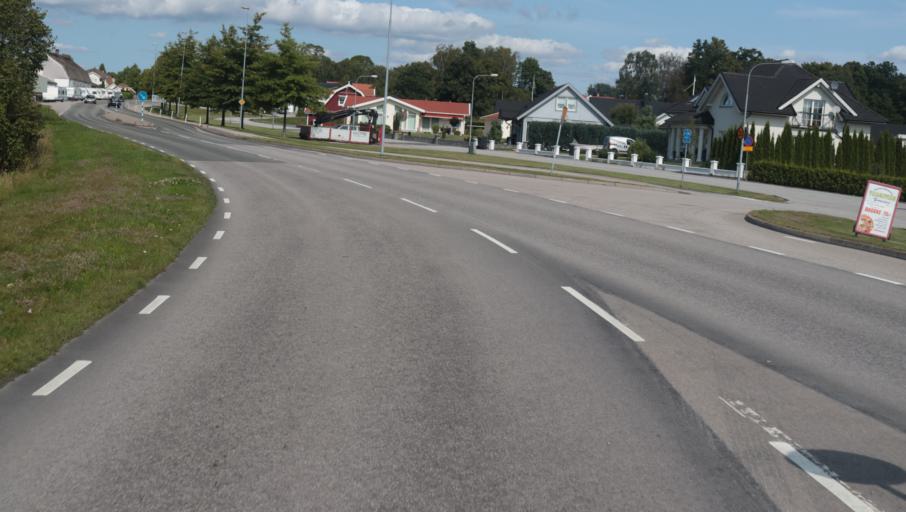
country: SE
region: Blekinge
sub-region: Karlshamns Kommun
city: Karlshamn
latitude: 56.1997
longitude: 14.8362
